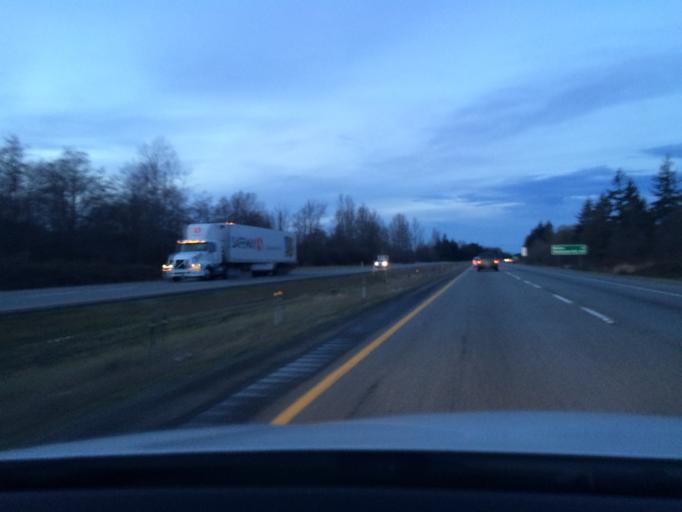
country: US
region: Washington
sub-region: Whatcom County
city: Ferndale
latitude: 48.8692
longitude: -122.5887
